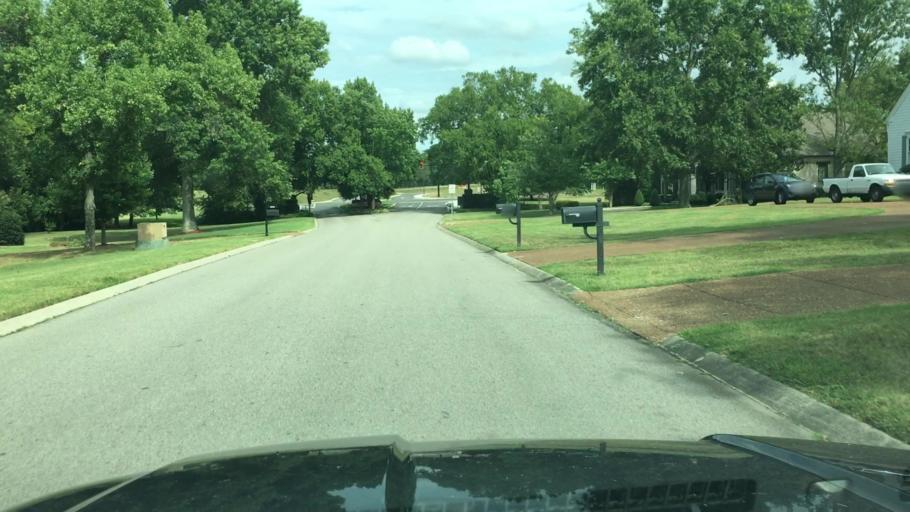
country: US
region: Tennessee
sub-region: Williamson County
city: Brentwood
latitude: 36.0190
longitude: -86.8226
